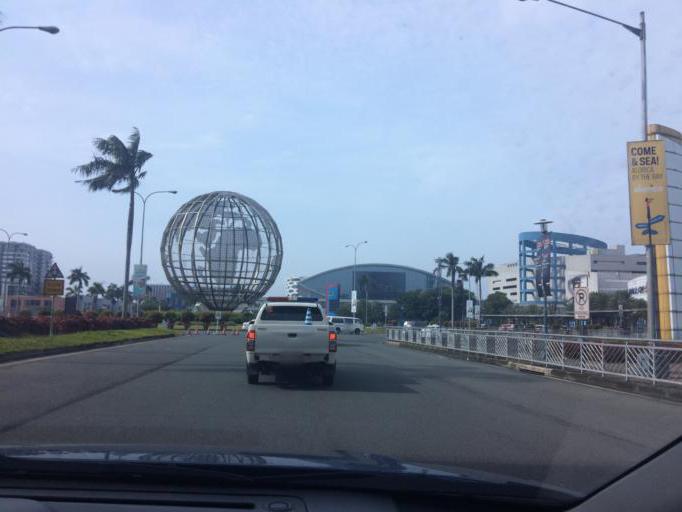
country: PH
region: Metro Manila
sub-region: City of Manila
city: Port Area
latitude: 14.5365
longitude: 120.9840
